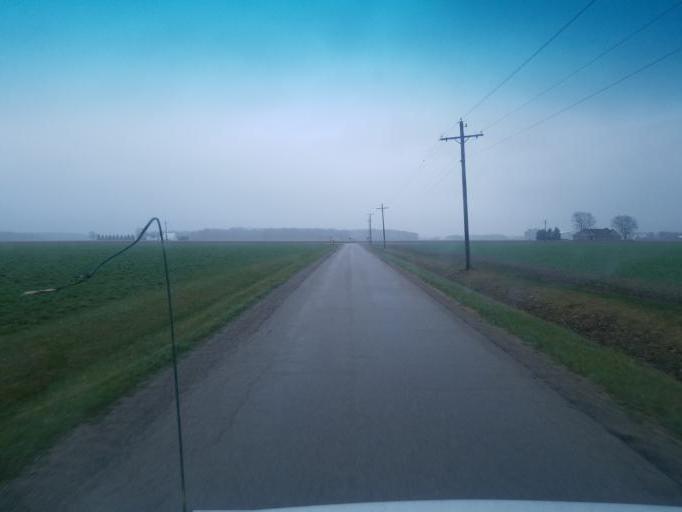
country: US
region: Ohio
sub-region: Fulton County
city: Archbold
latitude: 41.4134
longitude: -84.2477
